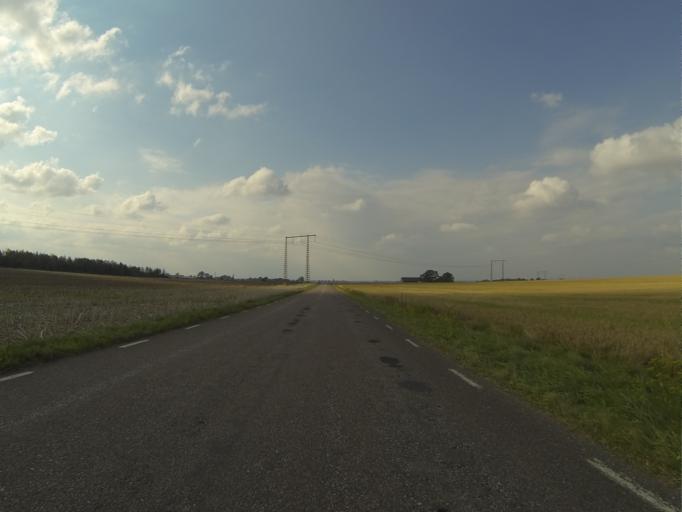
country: SE
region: Skane
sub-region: Lunds Kommun
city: Lund
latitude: 55.7520
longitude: 13.2238
